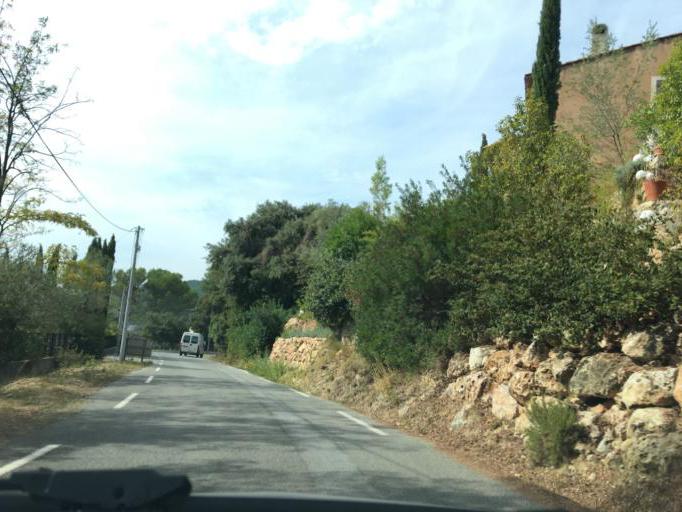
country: FR
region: Provence-Alpes-Cote d'Azur
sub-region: Departement du Var
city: Taradeau
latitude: 43.4565
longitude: 6.4301
